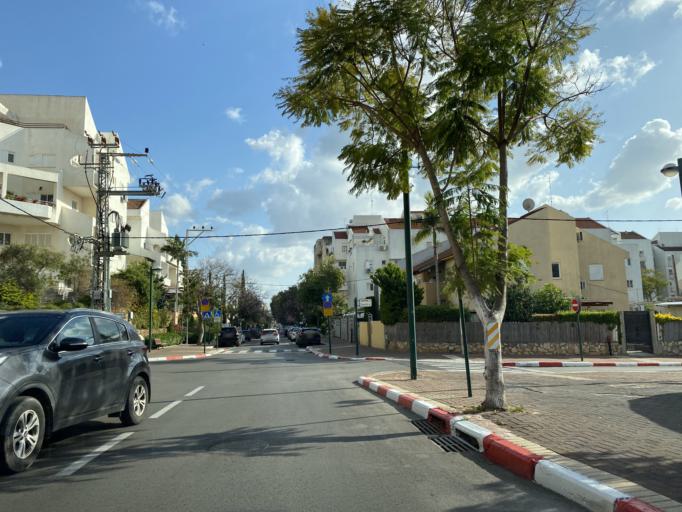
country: IL
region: Central District
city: Kfar Saba
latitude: 32.1807
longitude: 34.9191
